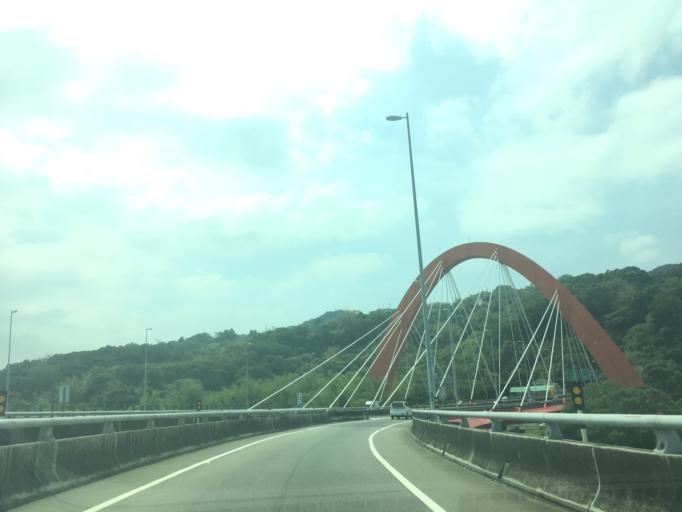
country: TW
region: Taiwan
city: Zhongxing New Village
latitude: 23.9575
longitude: 120.6538
